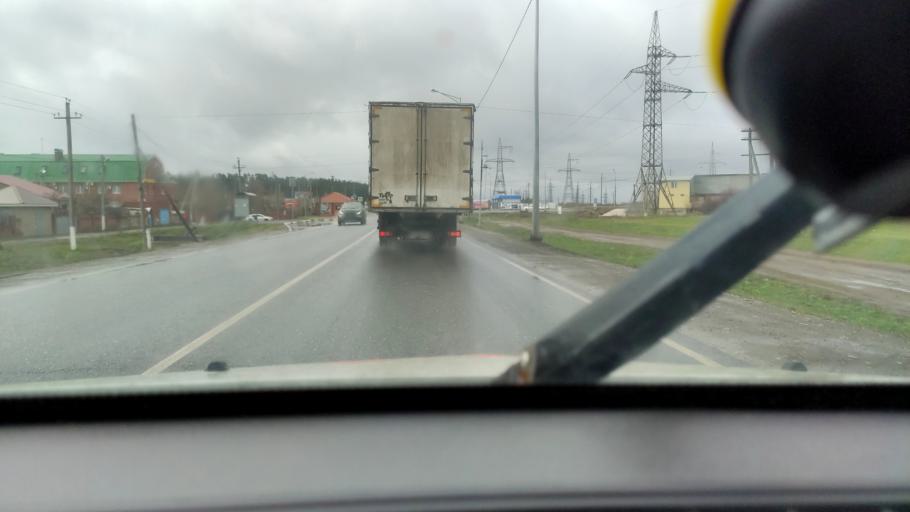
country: RU
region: Samara
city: Zhigulevsk
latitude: 53.5437
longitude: 49.5165
